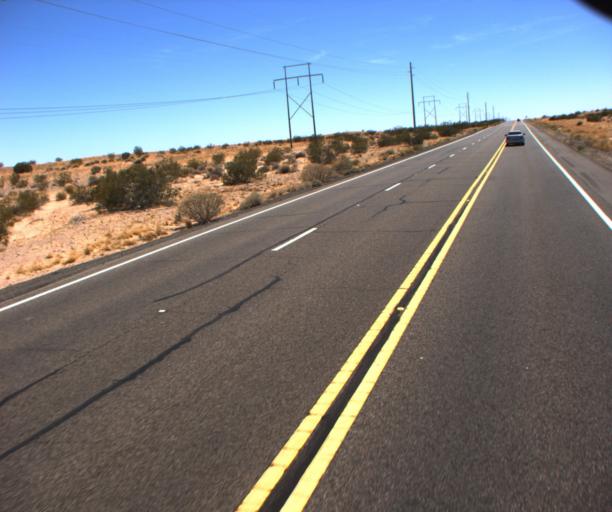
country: US
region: Arizona
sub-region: La Paz County
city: Parker
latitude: 33.9626
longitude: -114.2169
